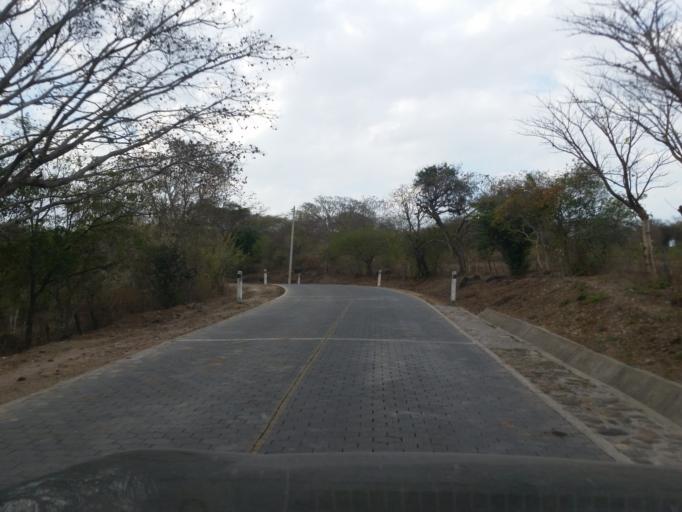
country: NI
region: Jinotega
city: La Concordia
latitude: 13.1765
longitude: -86.1680
